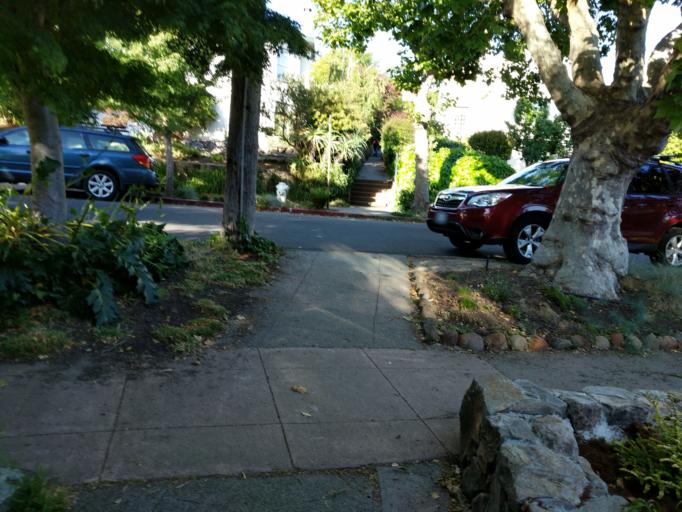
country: US
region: California
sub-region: Contra Costa County
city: Kensington
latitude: 37.8917
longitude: -122.2763
